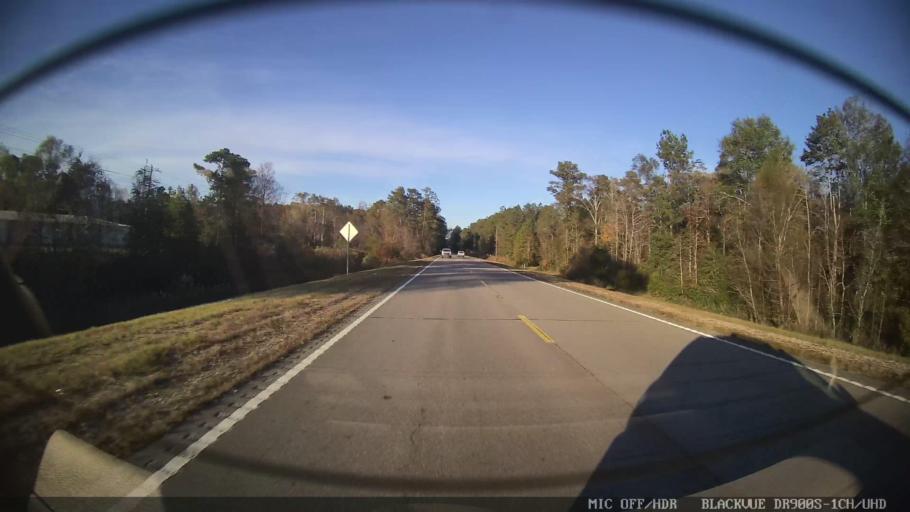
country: US
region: Mississippi
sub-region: Lamar County
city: Purvis
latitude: 31.0734
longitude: -89.4204
